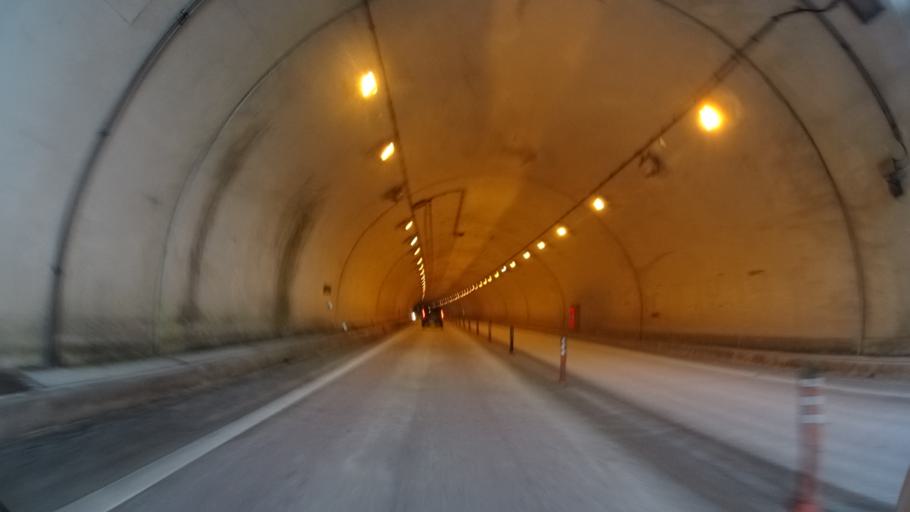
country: JP
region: Yamaguchi
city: Nagato
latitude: 34.3757
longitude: 131.2767
